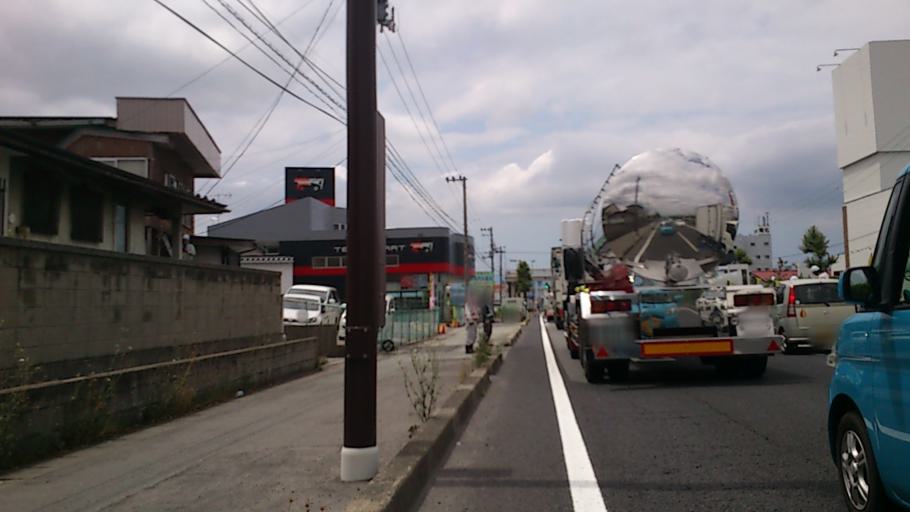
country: JP
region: Yamagata
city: Yamagata-shi
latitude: 38.2257
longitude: 140.3359
